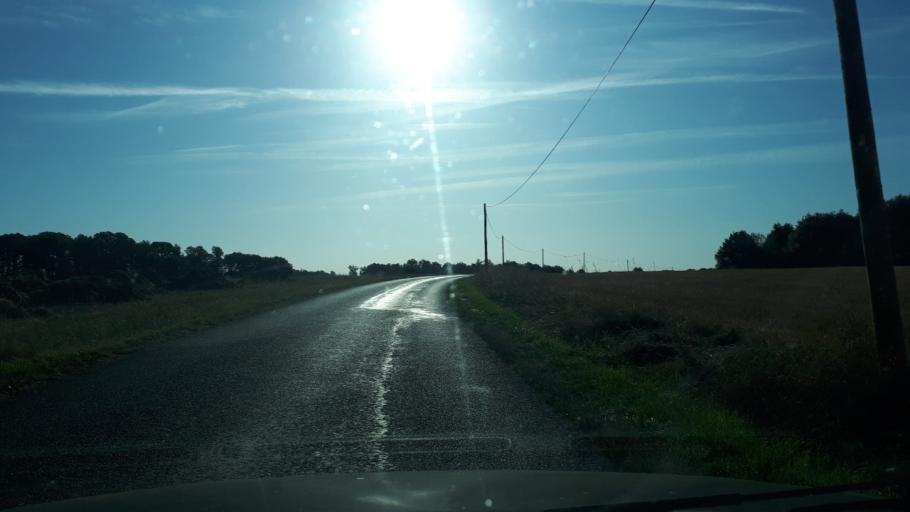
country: FR
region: Centre
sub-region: Departement d'Indre-et-Loire
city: Chateau-Renault
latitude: 47.6604
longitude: 0.9376
